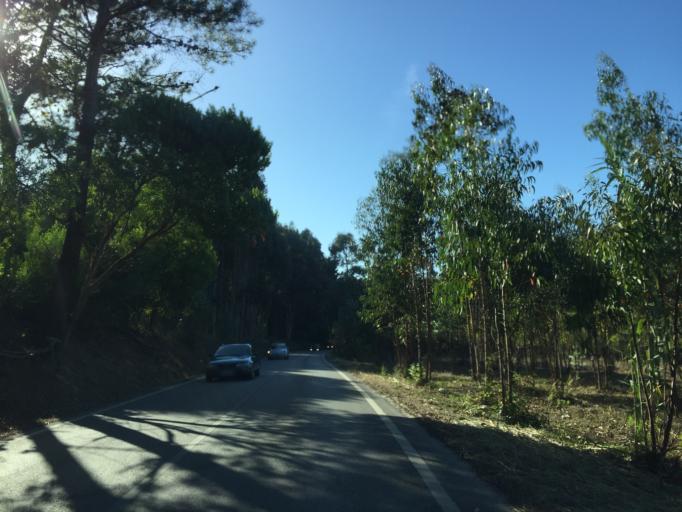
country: PT
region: Coimbra
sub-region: Figueira da Foz
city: Buarcos
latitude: 40.2156
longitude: -8.8724
